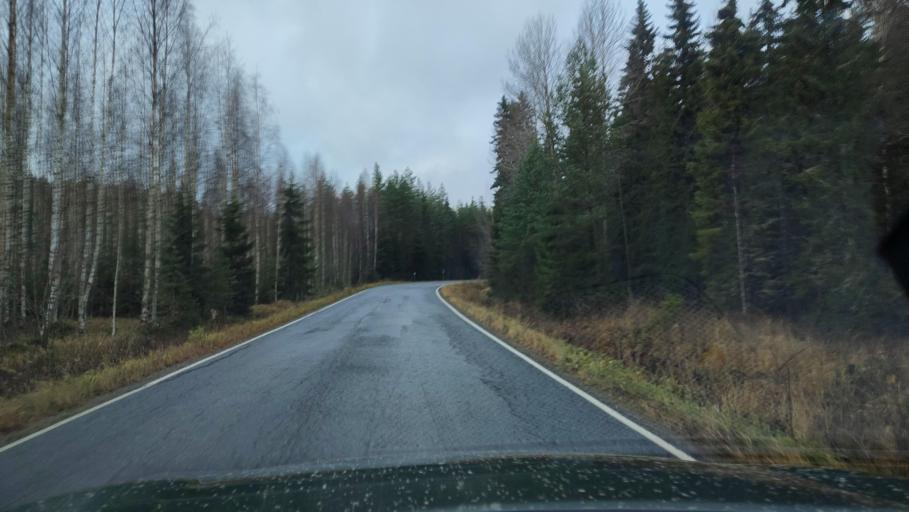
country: FI
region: Southern Ostrobothnia
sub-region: Suupohja
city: Karijoki
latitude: 62.4207
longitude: 21.5581
